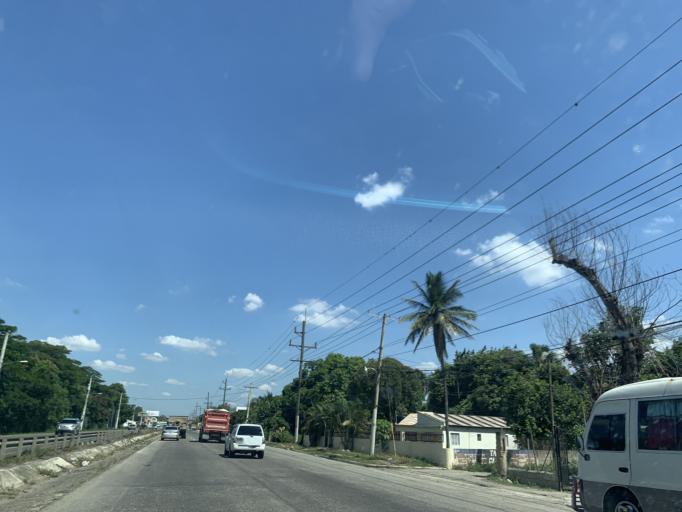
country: DO
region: Santiago
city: Villa Gonzalez
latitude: 19.5222
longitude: -70.7679
